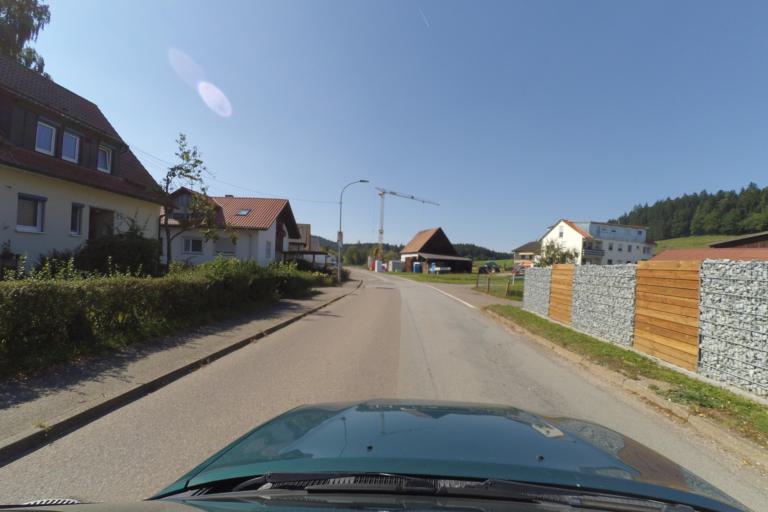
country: DE
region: Baden-Wuerttemberg
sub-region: Regierungsbezirk Stuttgart
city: Ruppertshofen
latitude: 48.8923
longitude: 9.7972
